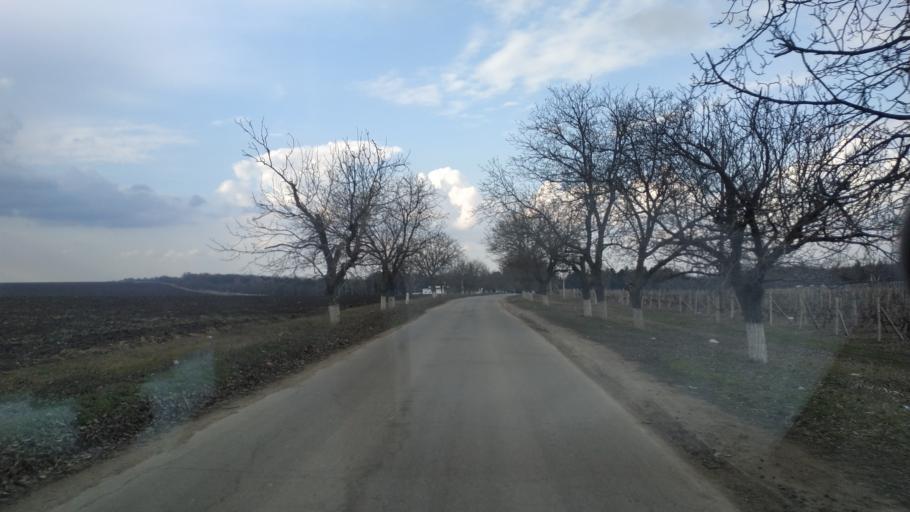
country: MD
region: Anenii Noi
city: Varnita
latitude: 46.8532
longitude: 29.3503
